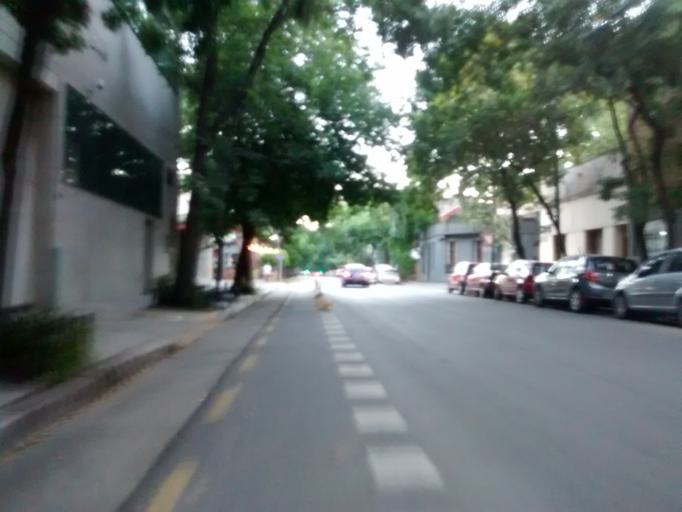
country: AR
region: Buenos Aires F.D.
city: Colegiales
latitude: -34.6033
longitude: -58.4502
